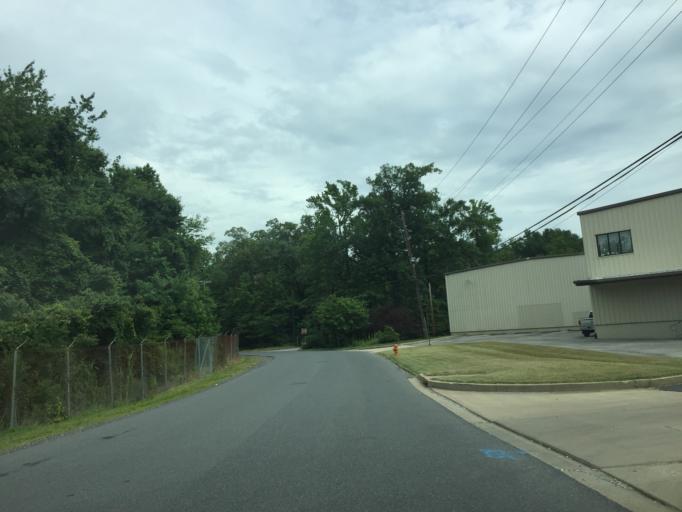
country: US
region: Maryland
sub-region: Baltimore County
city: Edgemere
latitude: 39.2722
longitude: -76.4593
